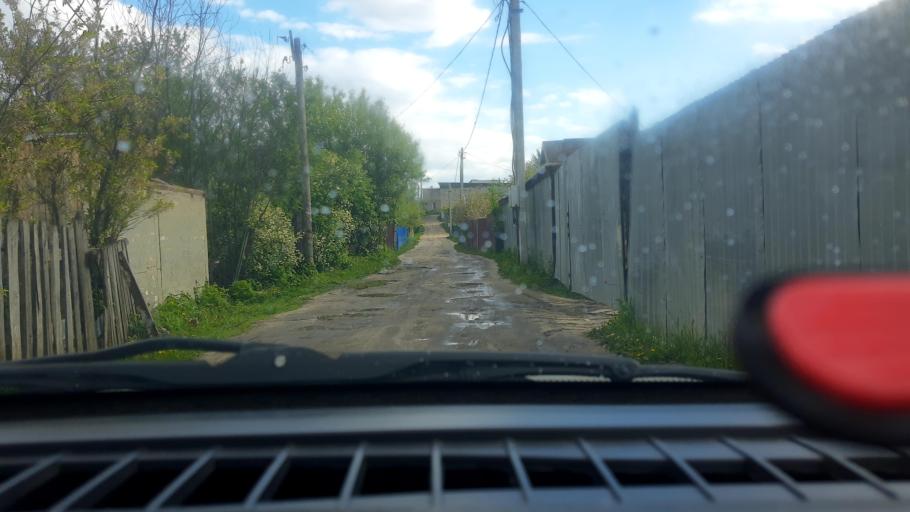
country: RU
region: Nizjnij Novgorod
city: Nizhniy Novgorod
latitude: 56.2668
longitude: 43.9539
